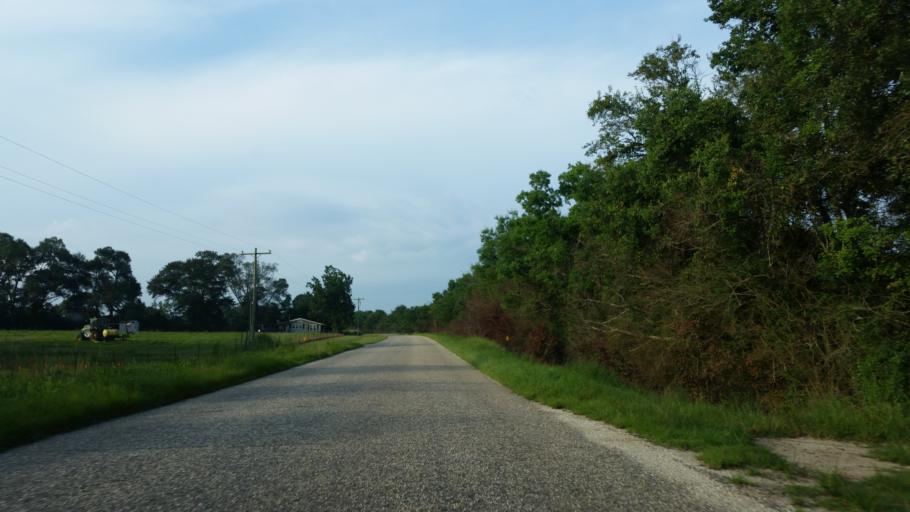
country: US
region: Alabama
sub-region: Escambia County
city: Atmore
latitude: 31.0067
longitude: -87.5683
